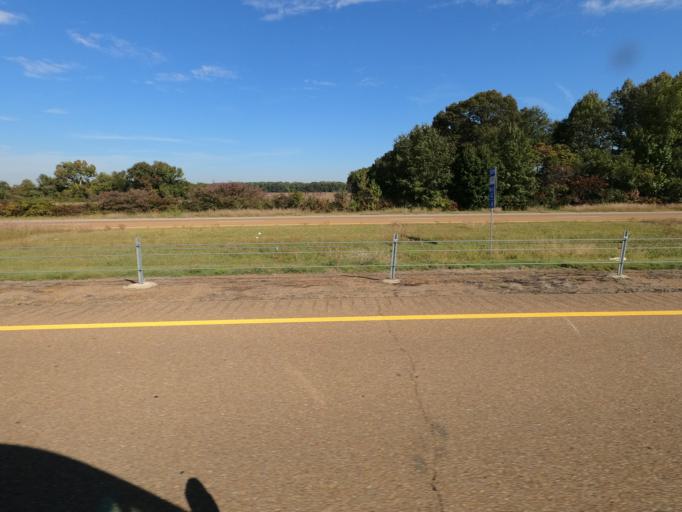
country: US
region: Tennessee
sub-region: Shelby County
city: Millington
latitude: 35.3083
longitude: -89.8093
